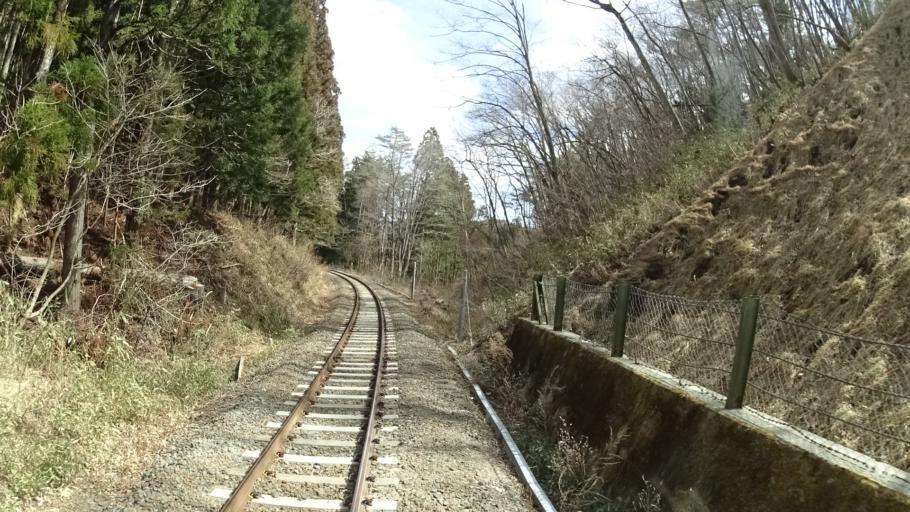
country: JP
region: Iwate
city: Yamada
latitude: 39.4750
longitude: 141.9306
